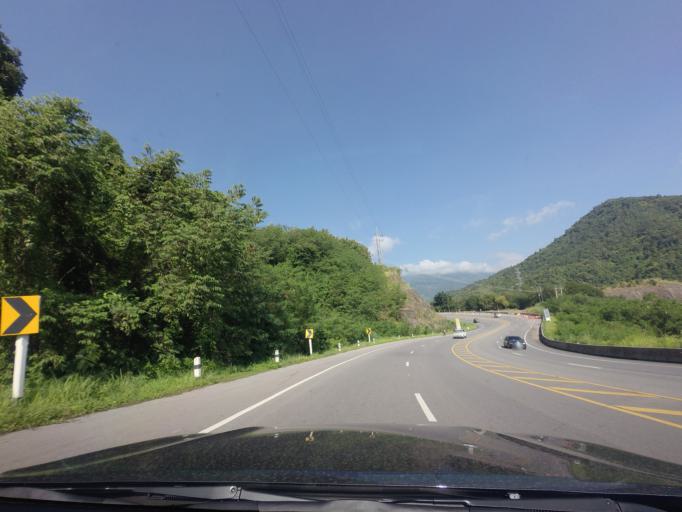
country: TH
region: Phetchabun
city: Lom Sak
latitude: 16.7801
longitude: 101.1050
